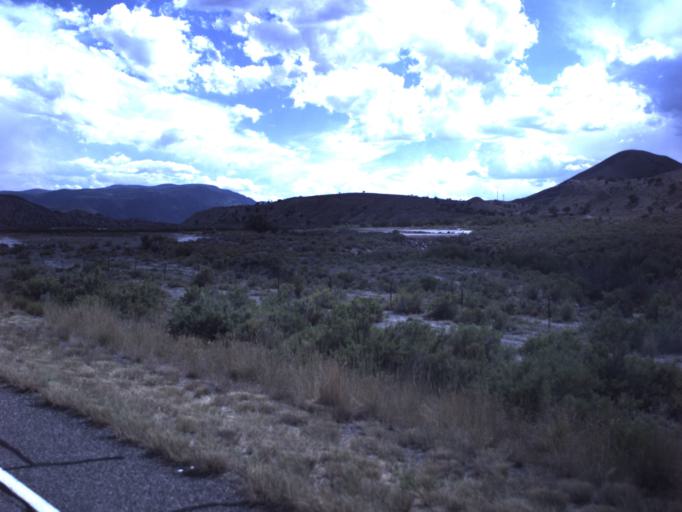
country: US
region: Utah
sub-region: Sevier County
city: Aurora
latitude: 38.8235
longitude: -111.9419
